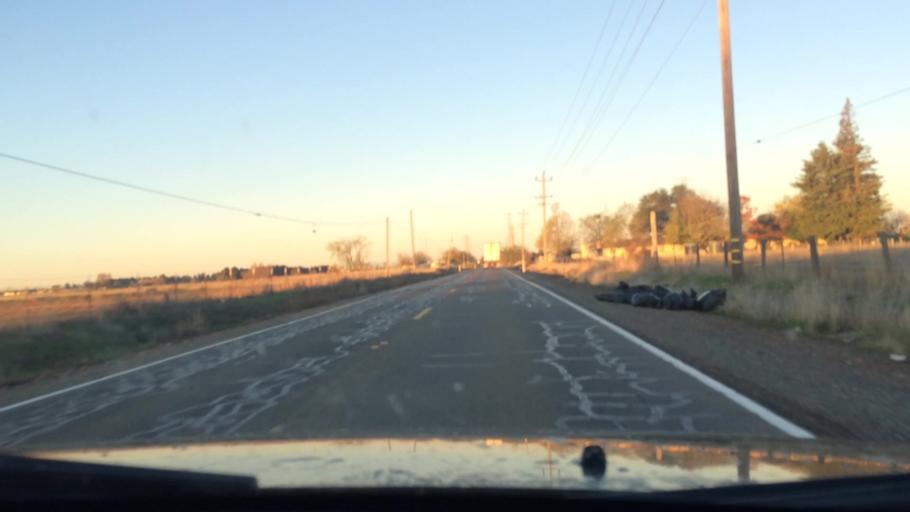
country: US
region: California
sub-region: Sacramento County
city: Vineyard
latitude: 38.5109
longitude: -121.3109
